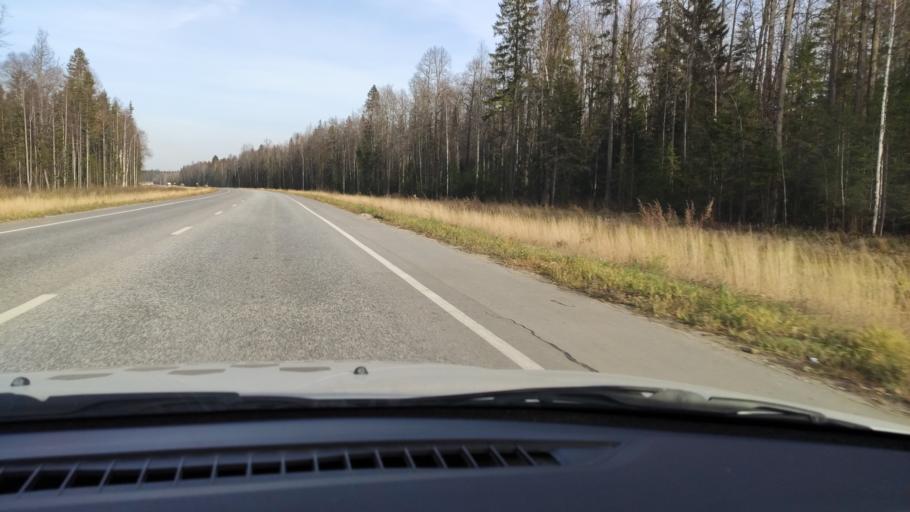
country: RU
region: Perm
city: Novyye Lyady
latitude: 58.0401
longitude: 56.5394
